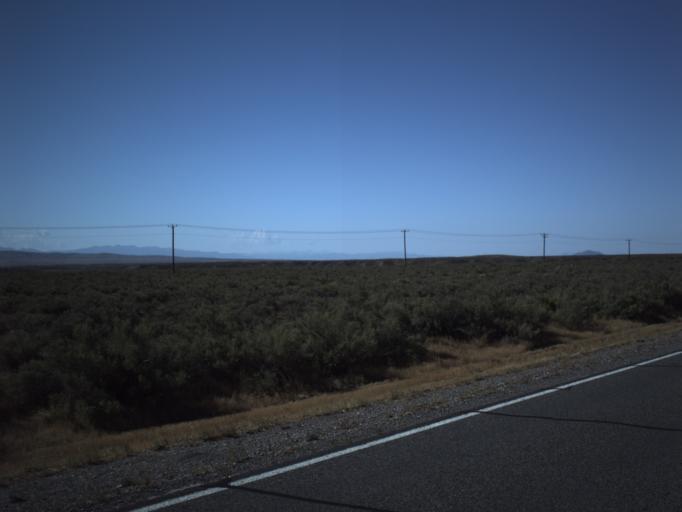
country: US
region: Utah
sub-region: Millard County
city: Delta
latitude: 39.4791
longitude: -112.4148
